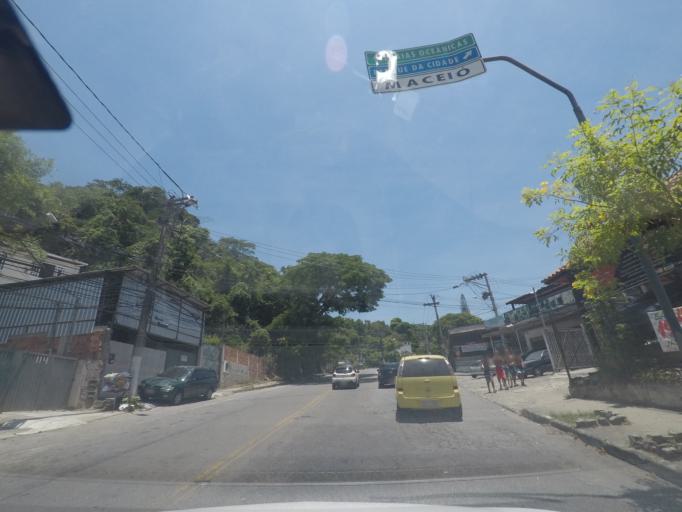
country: BR
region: Rio de Janeiro
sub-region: Niteroi
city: Niteroi
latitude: -22.9113
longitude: -43.0674
